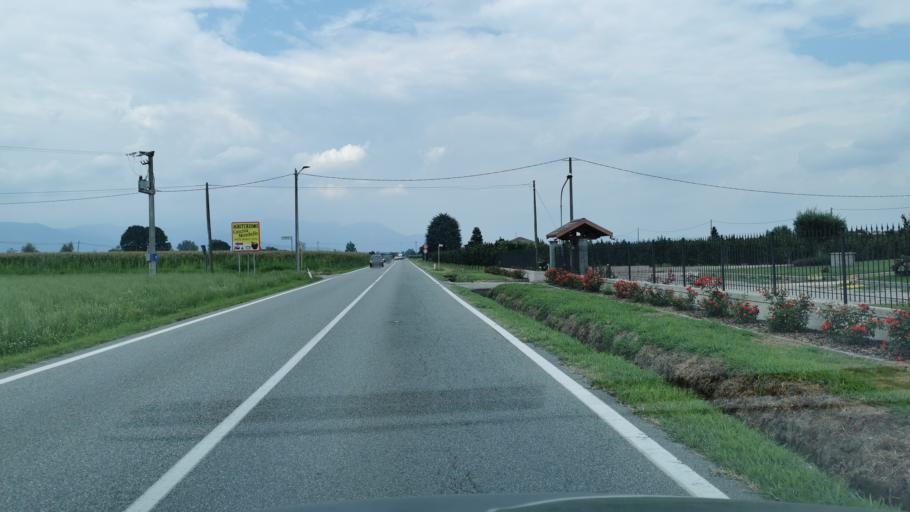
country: IT
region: Piedmont
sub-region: Provincia di Torino
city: Cavour
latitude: 44.8082
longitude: 7.3725
